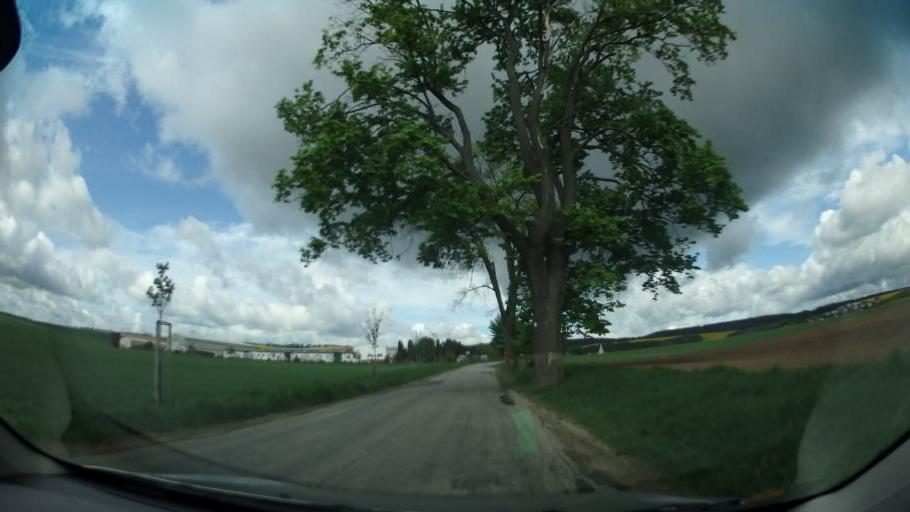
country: CZ
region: South Moravian
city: Ricany
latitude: 49.2293
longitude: 16.4137
